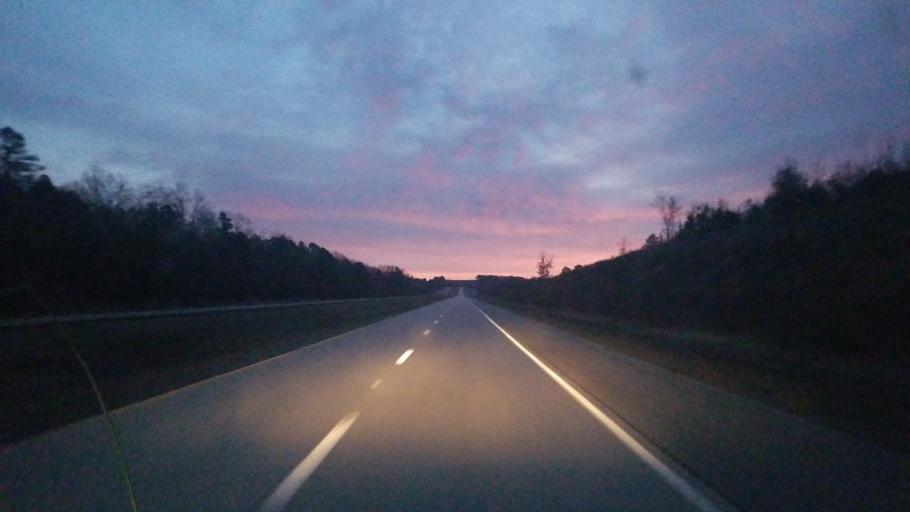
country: US
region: Missouri
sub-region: Shannon County
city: Winona
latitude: 36.9975
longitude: -91.4447
